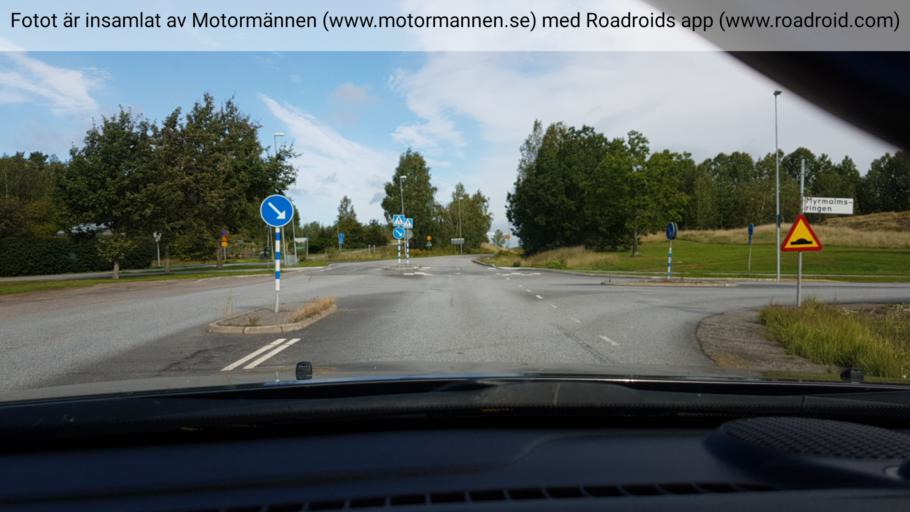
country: SE
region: Stockholm
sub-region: Haninge Kommun
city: Haninge
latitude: 59.1815
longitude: 18.1603
